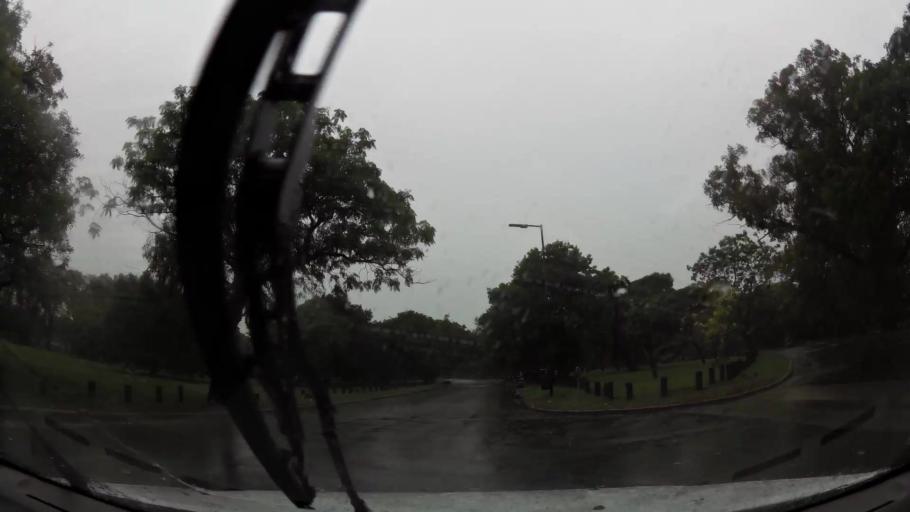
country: AR
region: Buenos Aires F.D.
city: Colegiales
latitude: -34.5630
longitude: -58.4258
